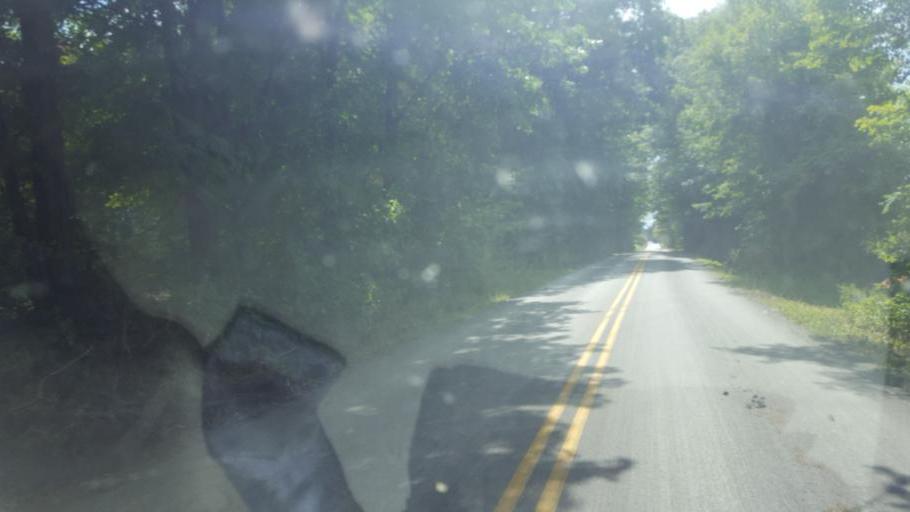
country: US
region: Pennsylvania
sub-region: Mercer County
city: Greenville
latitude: 41.4970
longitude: -80.3383
